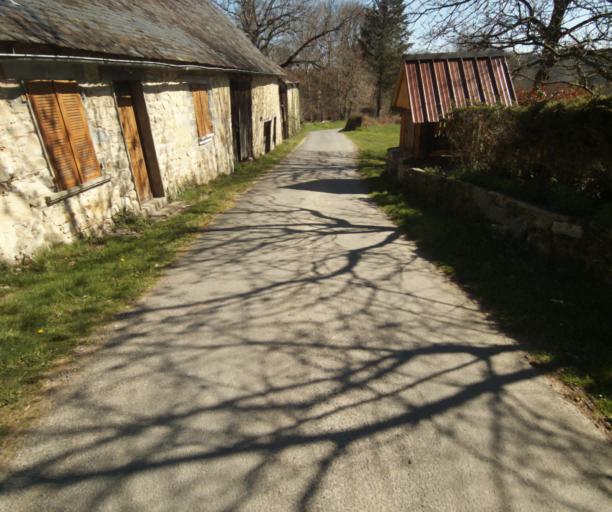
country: FR
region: Limousin
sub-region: Departement de la Correze
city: Saint-Mexant
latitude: 45.3040
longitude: 1.6227
